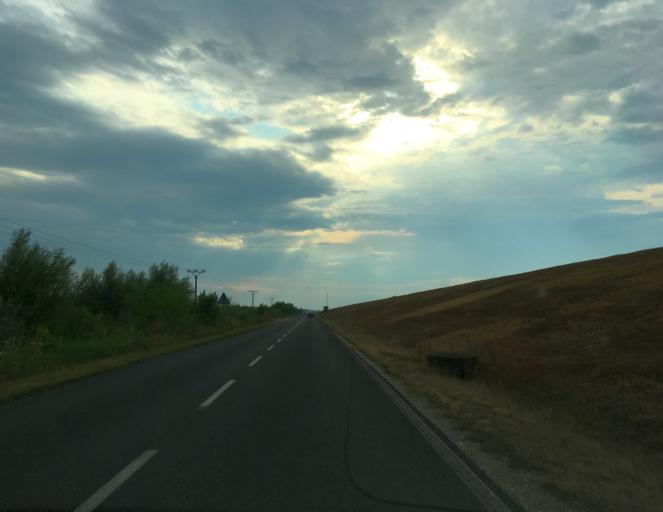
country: SK
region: Trnavsky
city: Samorin
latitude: 47.9979
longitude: 17.3184
